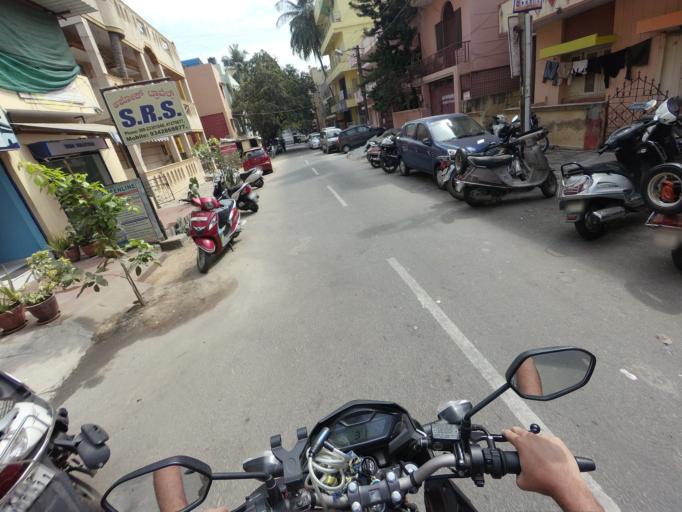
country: IN
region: Karnataka
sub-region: Bangalore Urban
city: Bangalore
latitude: 12.9725
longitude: 77.5402
